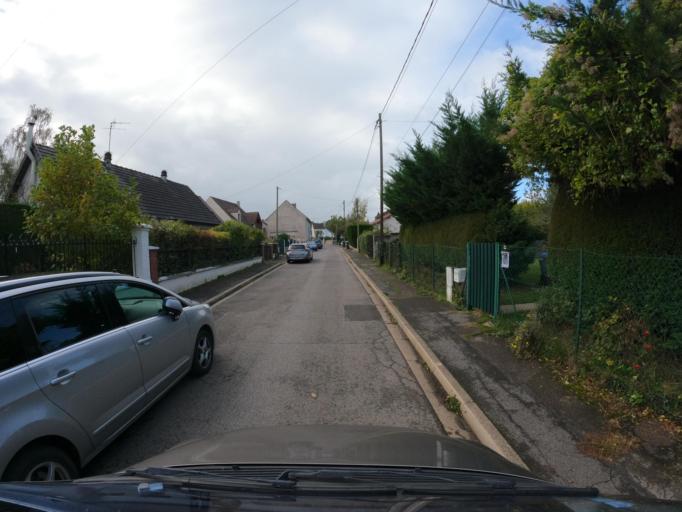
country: FR
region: Ile-de-France
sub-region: Departement de Seine-et-Marne
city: Saint-Germain-sur-Morin
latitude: 48.8804
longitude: 2.8547
